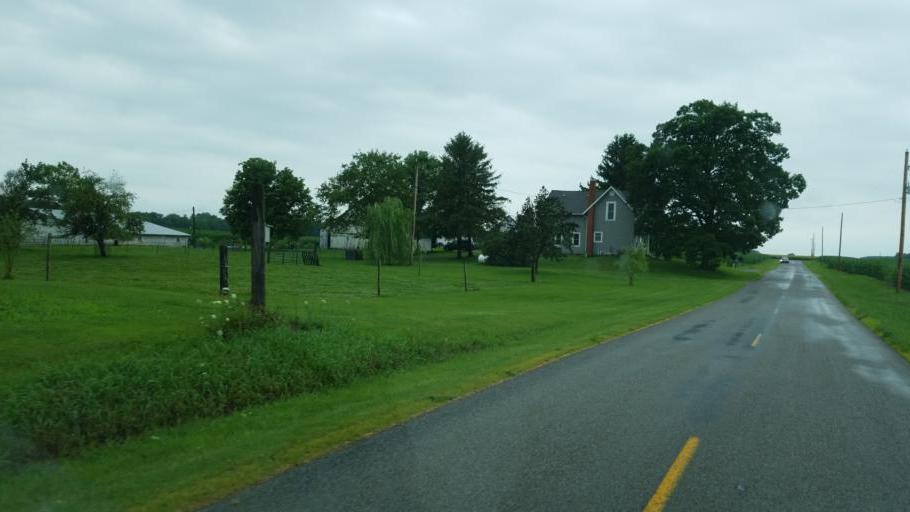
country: US
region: Ohio
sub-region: Hardin County
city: Kenton
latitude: 40.5088
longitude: -83.4955
